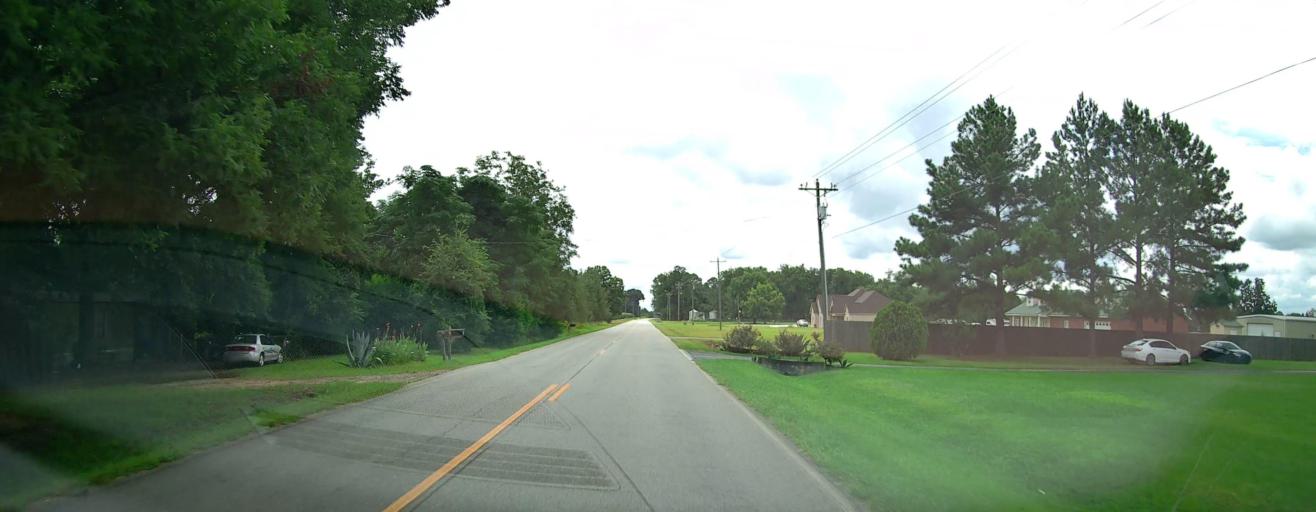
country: US
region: Georgia
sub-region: Peach County
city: Byron
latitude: 32.5606
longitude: -83.7534
